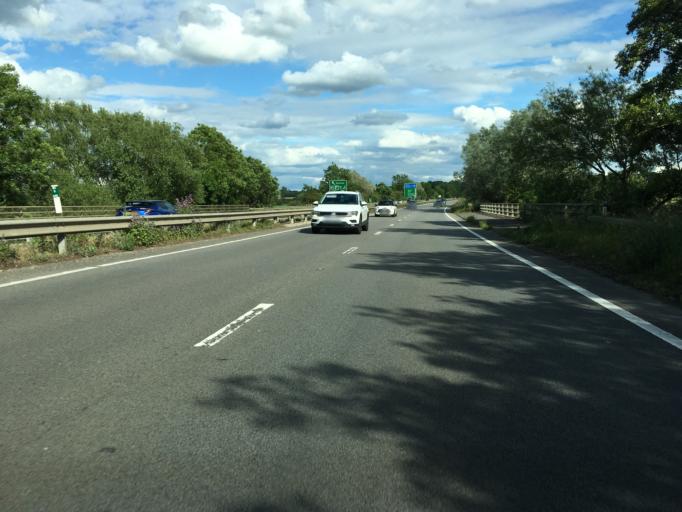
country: GB
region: England
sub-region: Oxfordshire
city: Wheatley
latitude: 51.7449
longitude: -1.1155
